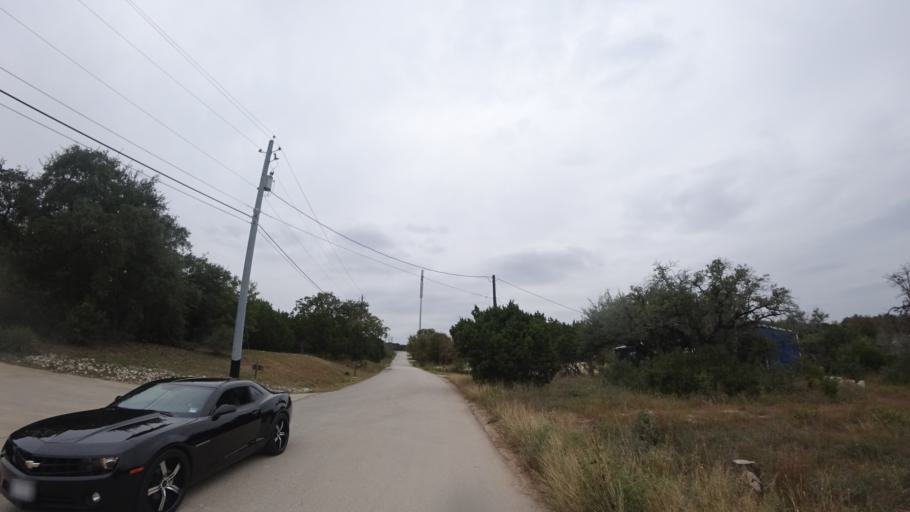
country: US
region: Texas
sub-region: Travis County
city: Hudson Bend
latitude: 30.3843
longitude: -97.9393
